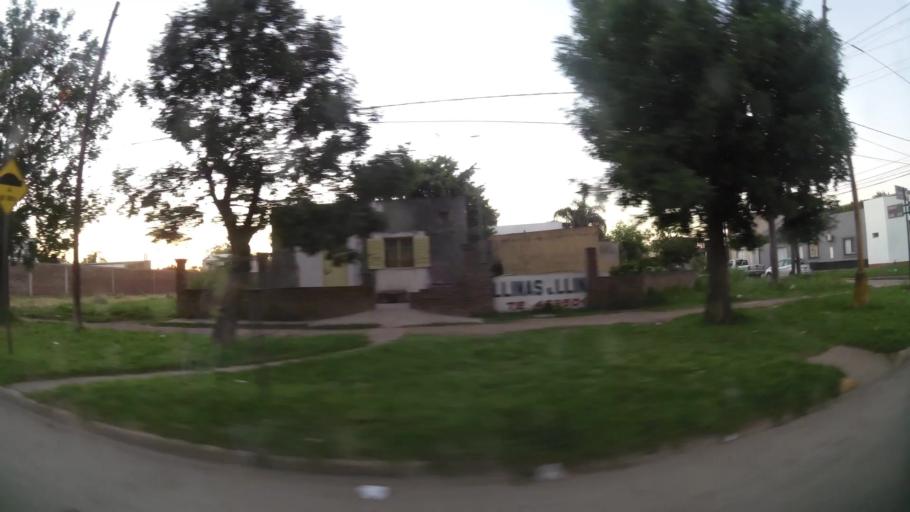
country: AR
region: Santa Fe
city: Santa Fe de la Vera Cruz
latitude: -31.6002
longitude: -60.7016
